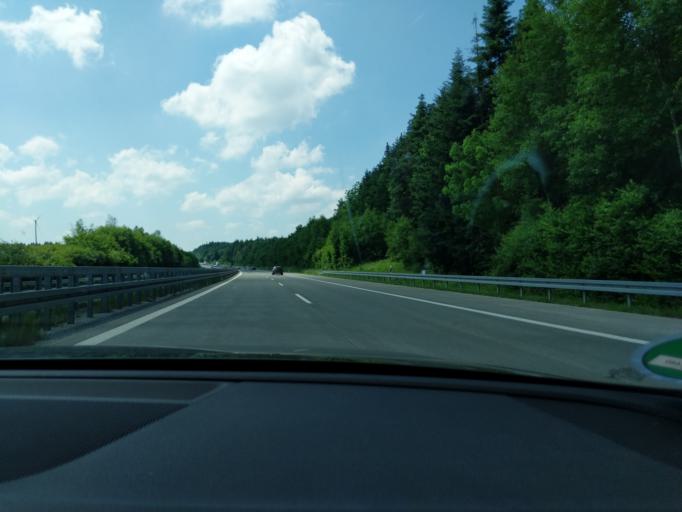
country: DE
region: Baden-Wuerttemberg
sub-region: Regierungsbezirk Stuttgart
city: Buch am Ahorn
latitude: 49.5296
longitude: 9.5757
